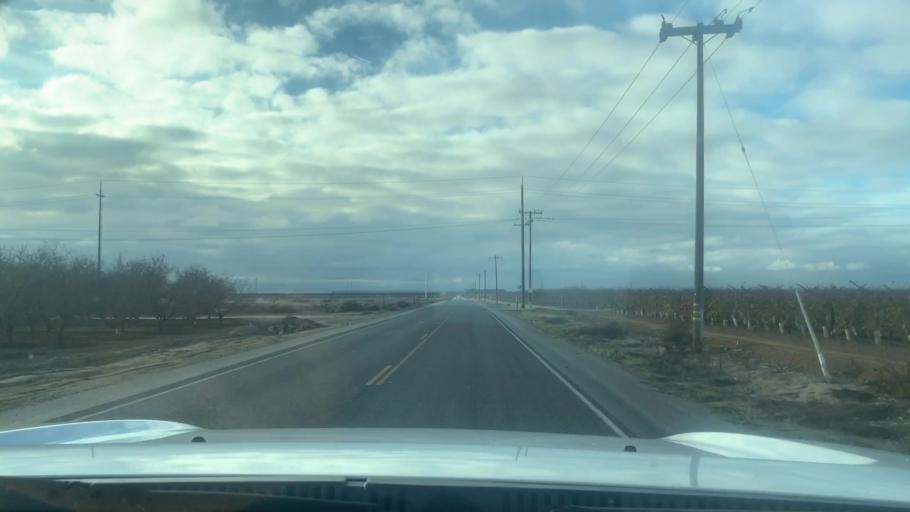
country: US
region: California
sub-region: Kern County
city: Buttonwillow
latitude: 35.5006
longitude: -119.4384
